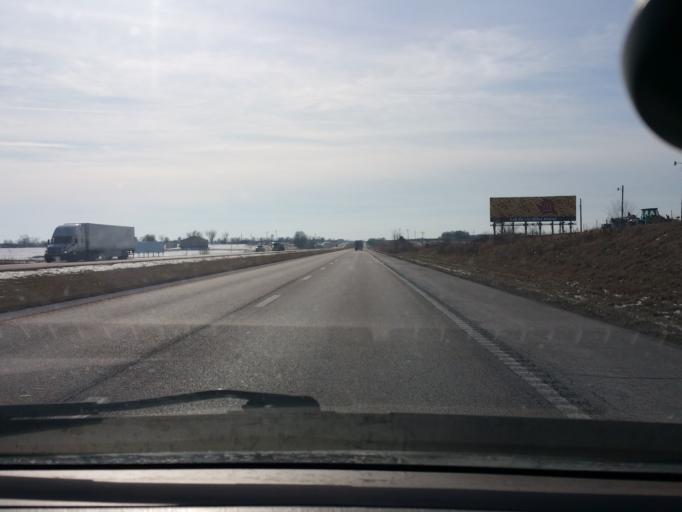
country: US
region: Missouri
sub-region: Clinton County
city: Lathrop
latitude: 39.5461
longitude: -94.2723
